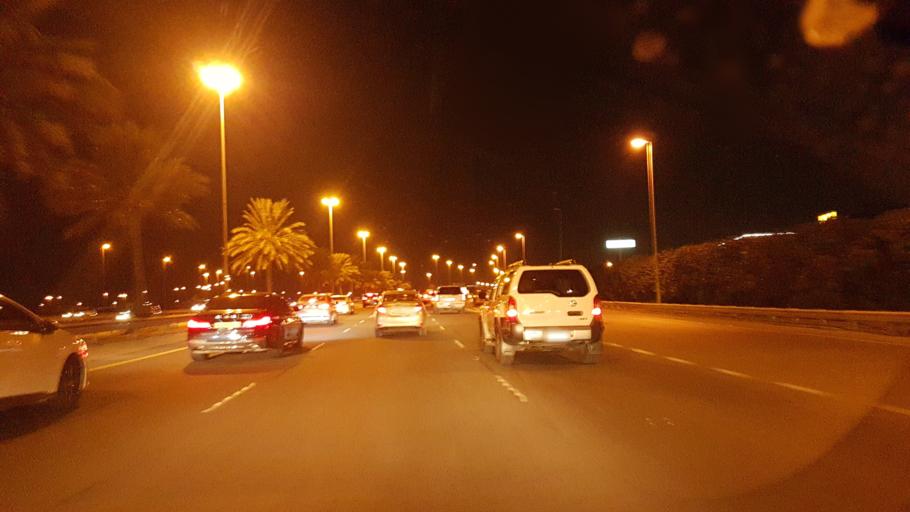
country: BH
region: Northern
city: Madinat `Isa
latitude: 26.1773
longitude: 50.5024
